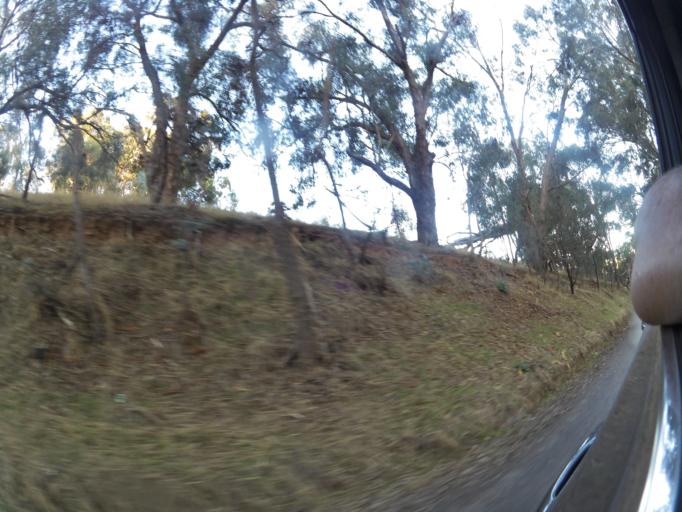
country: AU
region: Victoria
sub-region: Murrindindi
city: Alexandra
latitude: -37.1478
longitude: 145.5231
